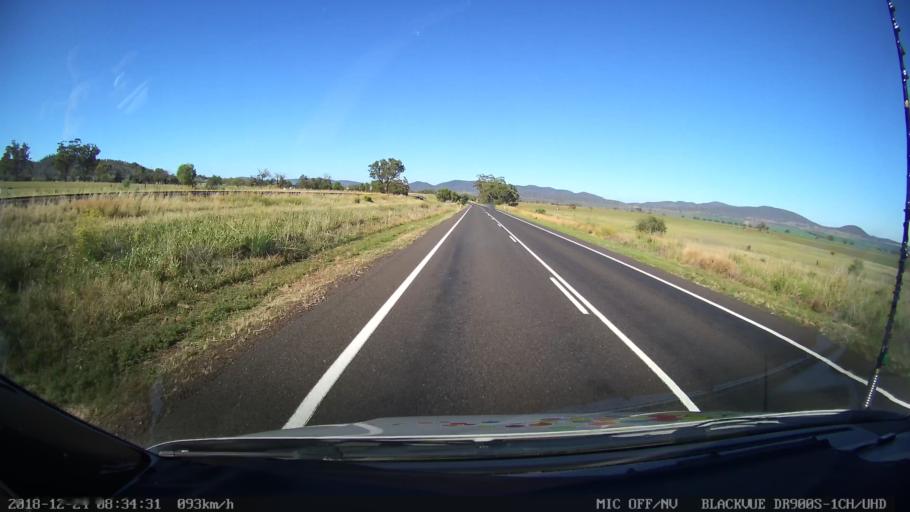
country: AU
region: New South Wales
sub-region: Liverpool Plains
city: Quirindi
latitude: -31.2934
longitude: 150.6702
